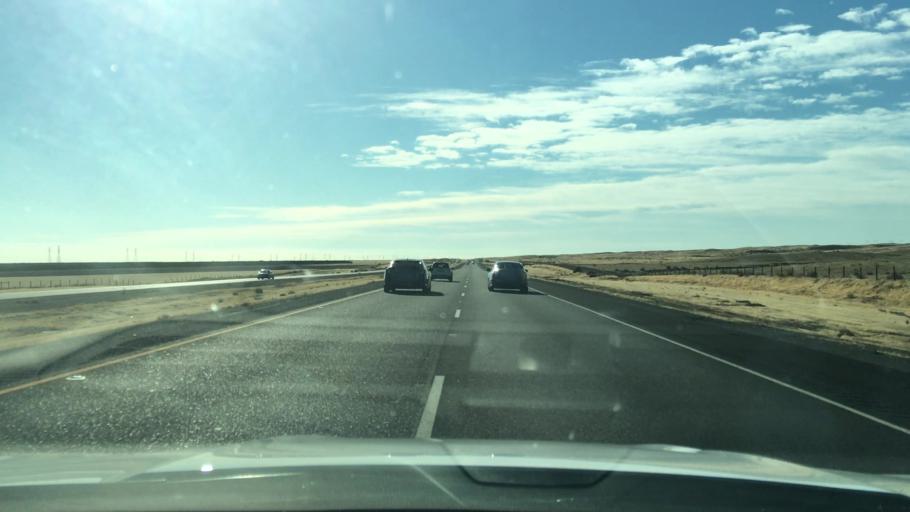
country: US
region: California
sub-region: Fresno County
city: Mendota
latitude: 36.5508
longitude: -120.5147
